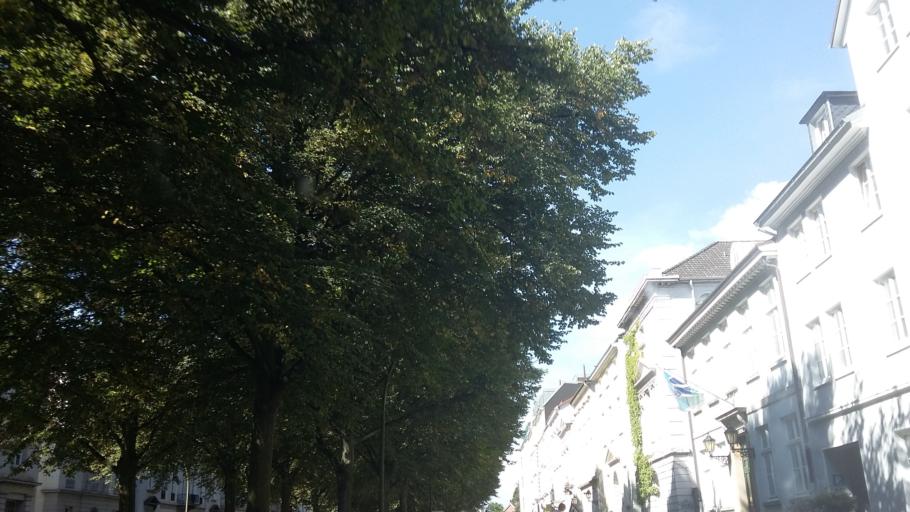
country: DE
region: Hamburg
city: Altona
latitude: 53.5465
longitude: 9.9391
